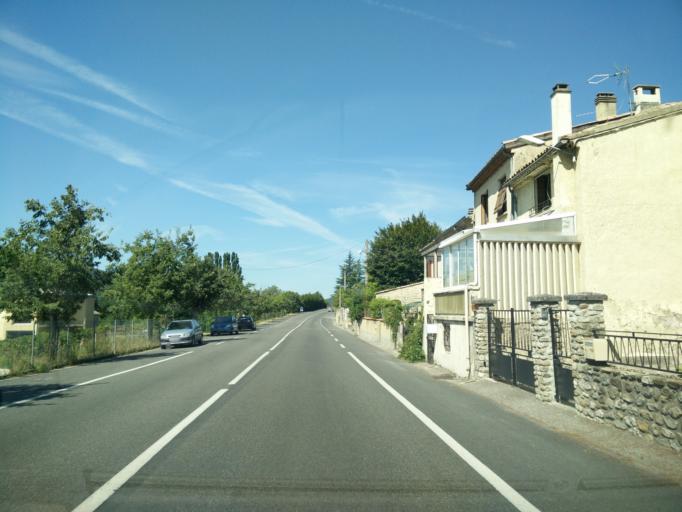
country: FR
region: Rhone-Alpes
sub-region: Departement de la Drome
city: Dieulefit
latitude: 44.5235
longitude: 5.0445
